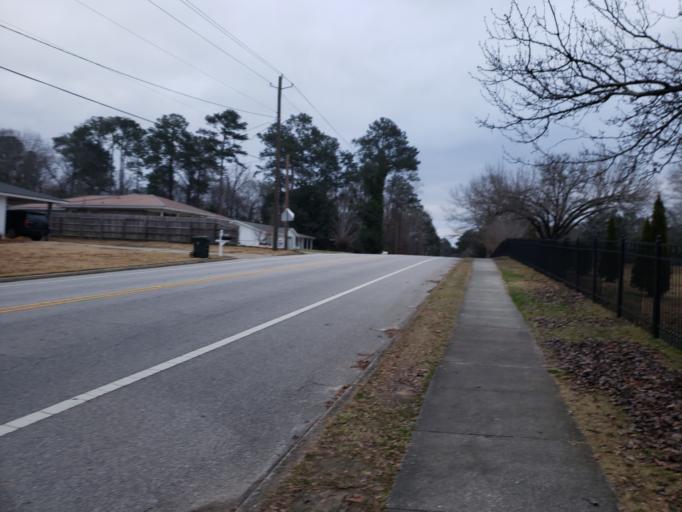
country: US
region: Alabama
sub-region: Lee County
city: Auburn
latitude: 32.5989
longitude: -85.4610
